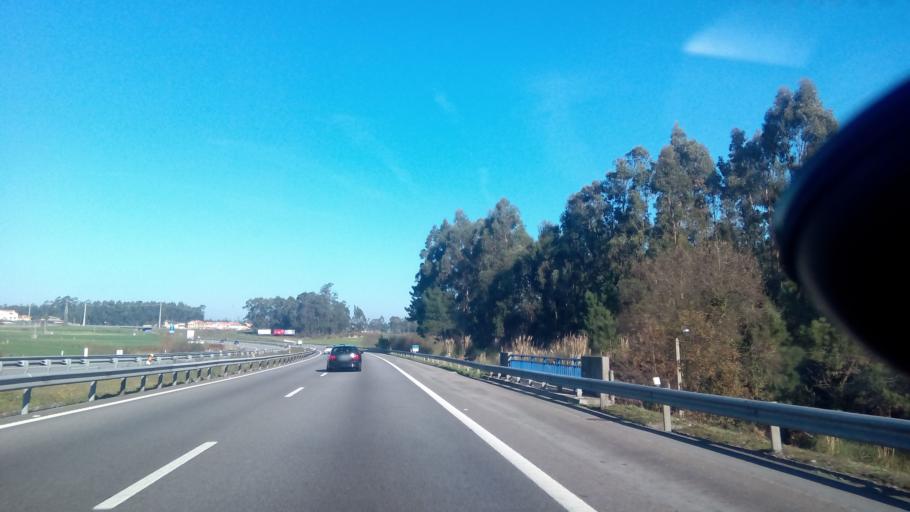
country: PT
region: Porto
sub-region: Matosinhos
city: Lavra
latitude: 41.2759
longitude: -8.7002
